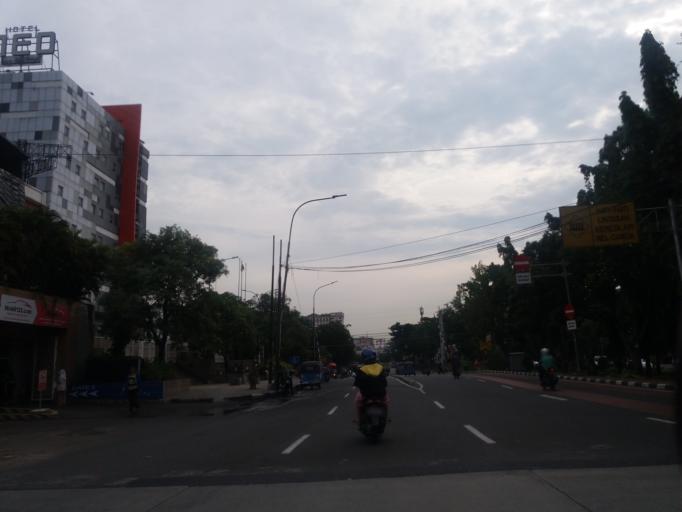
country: ID
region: Jakarta Raya
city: Jakarta
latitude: -6.1351
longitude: 106.8316
